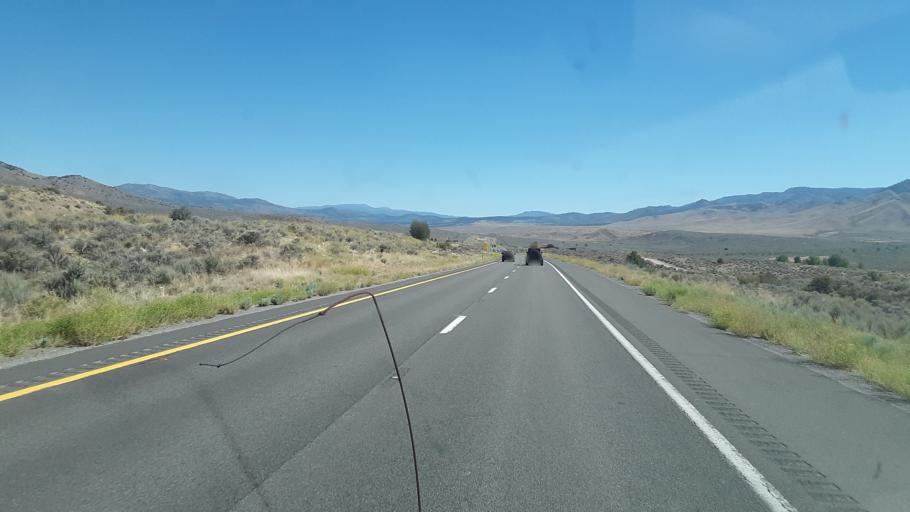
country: US
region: Nevada
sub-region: Washoe County
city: Cold Springs
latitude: 39.7445
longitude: -120.0398
